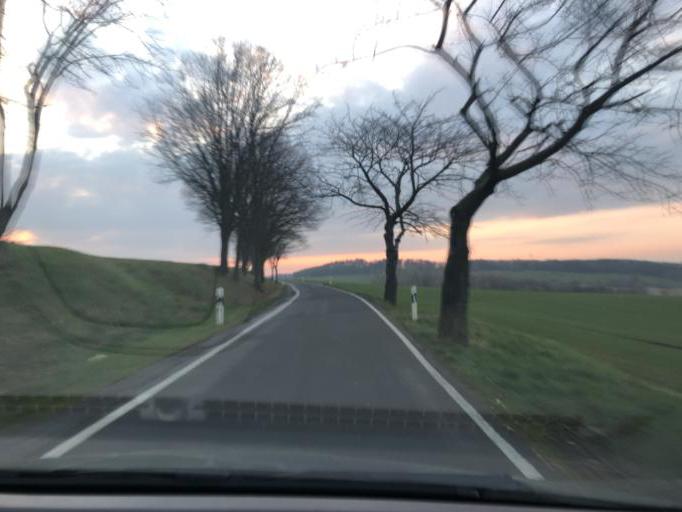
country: DE
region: Saxony
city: Kamenz
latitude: 51.2394
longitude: 14.0978
